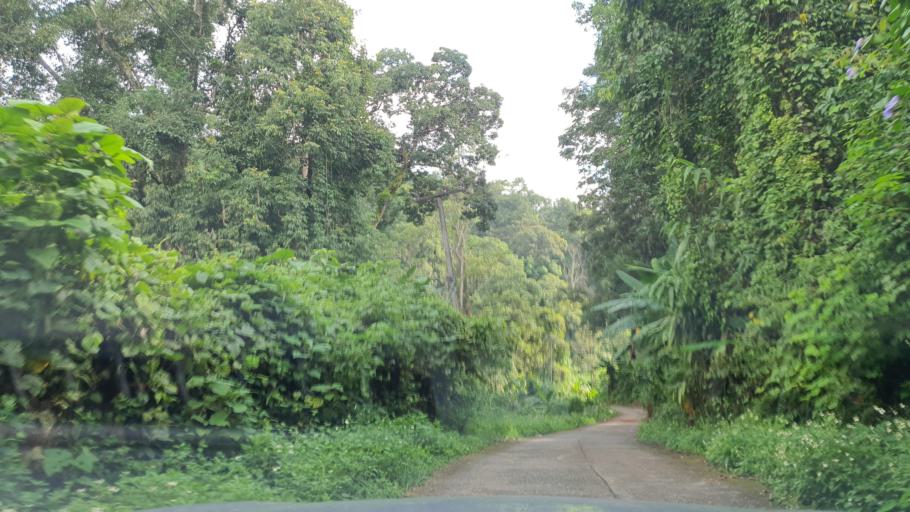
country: TH
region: Chiang Mai
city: Mae On
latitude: 18.9312
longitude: 99.3118
